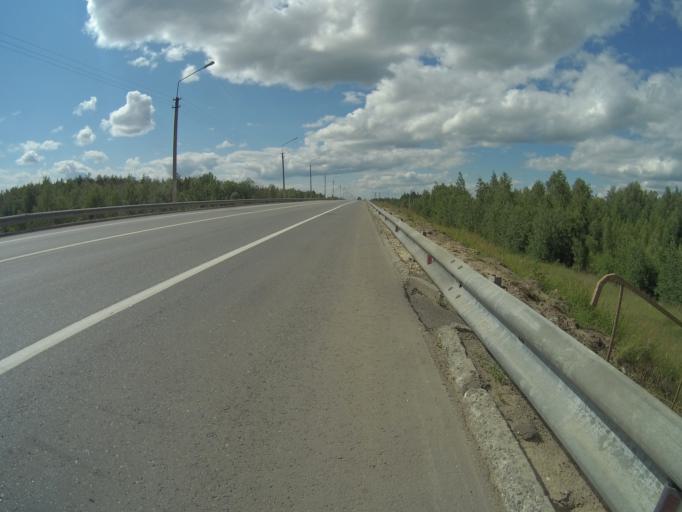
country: RU
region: Vladimir
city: Vorsha
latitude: 56.0744
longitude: 40.2167
